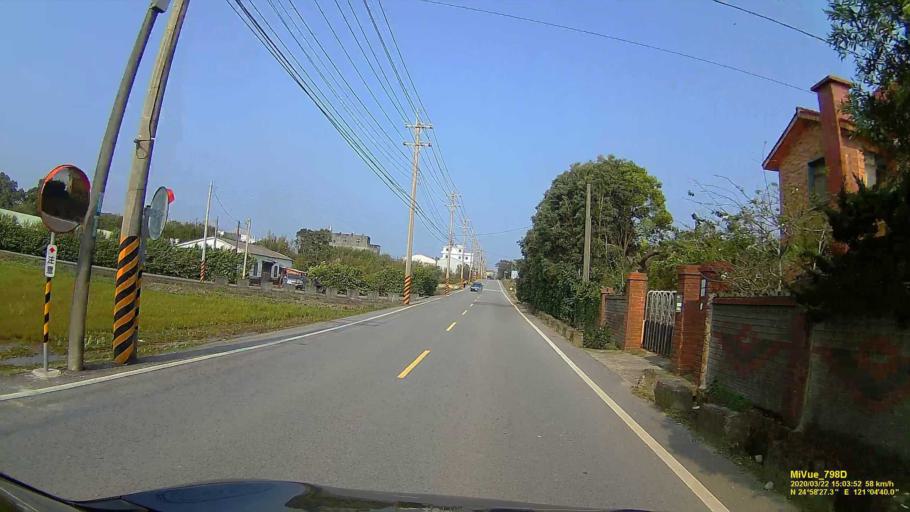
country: TW
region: Taiwan
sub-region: Hsinchu
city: Zhubei
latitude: 24.9745
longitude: 121.0783
